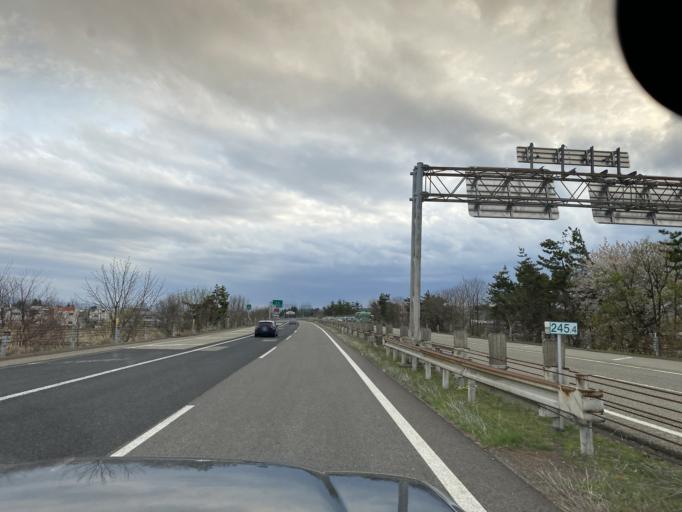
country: JP
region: Niigata
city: Nagaoka
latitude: 37.4535
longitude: 138.7892
